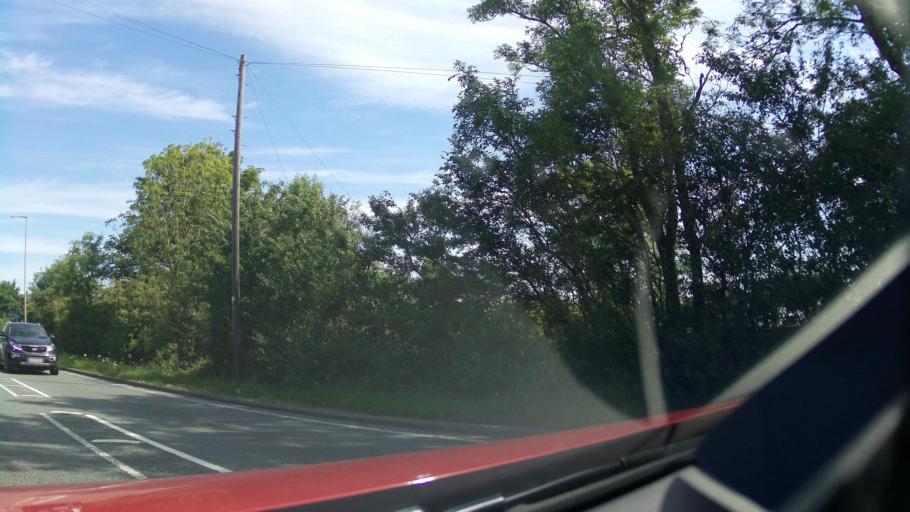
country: GB
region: England
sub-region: Lincolnshire
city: Burton
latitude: 53.2820
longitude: -0.5404
